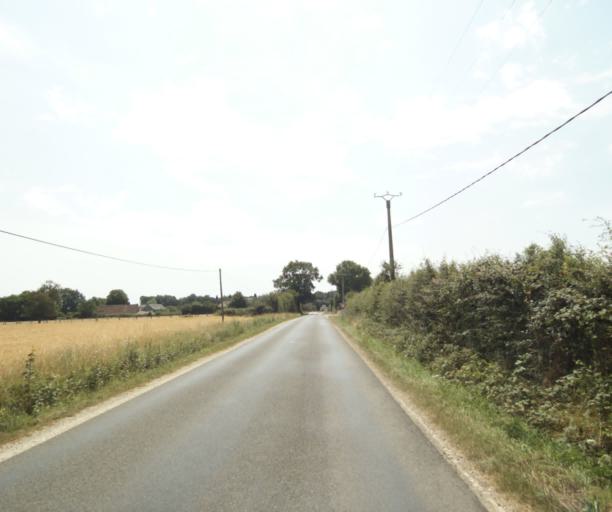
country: FR
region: Centre
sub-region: Departement d'Eure-et-Loir
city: La Bazoche-Gouet
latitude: 48.1782
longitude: 1.0146
